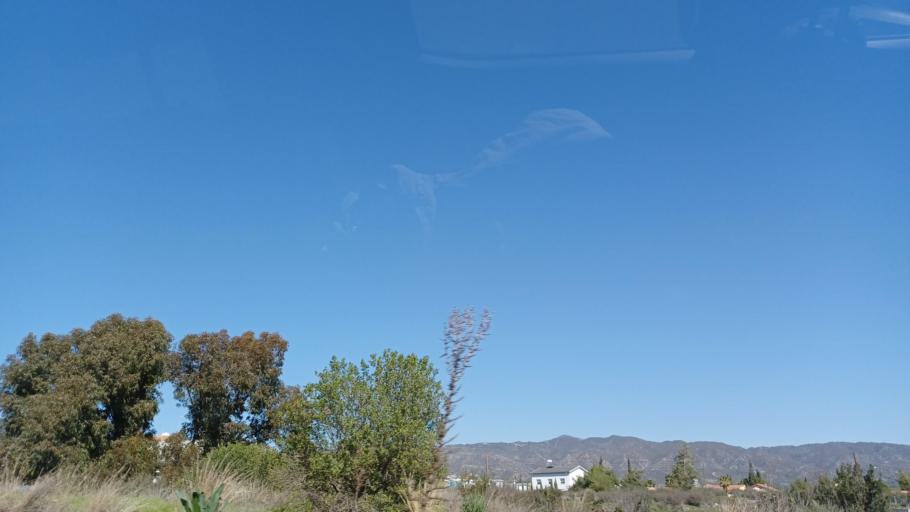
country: CY
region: Limassol
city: Parekklisha
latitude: 34.7489
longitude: 33.1546
